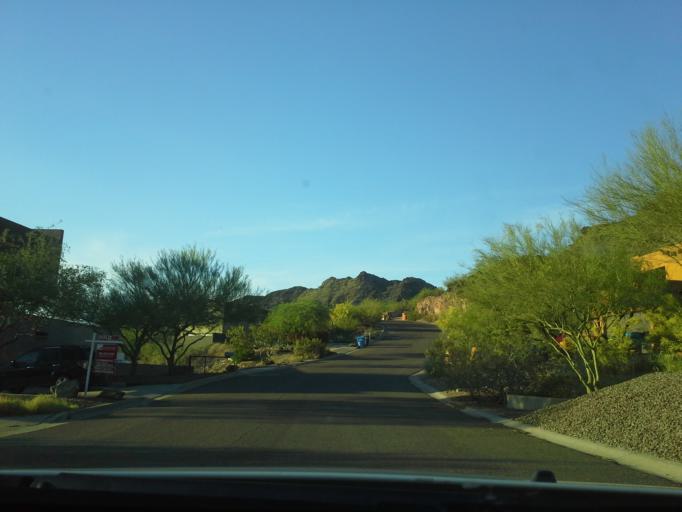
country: US
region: Arizona
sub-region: Maricopa County
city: Paradise Valley
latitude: 33.5719
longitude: -112.0427
